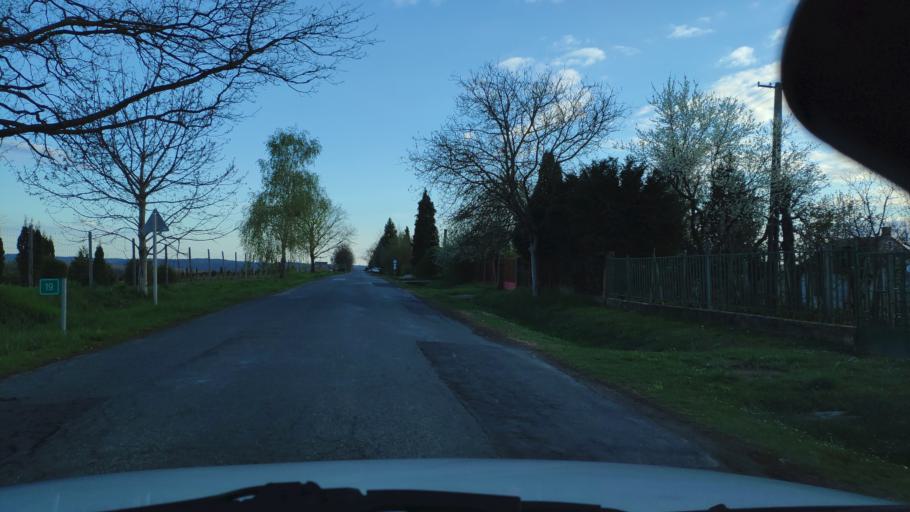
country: HU
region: Zala
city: Nagykanizsa
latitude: 46.4291
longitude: 17.0476
